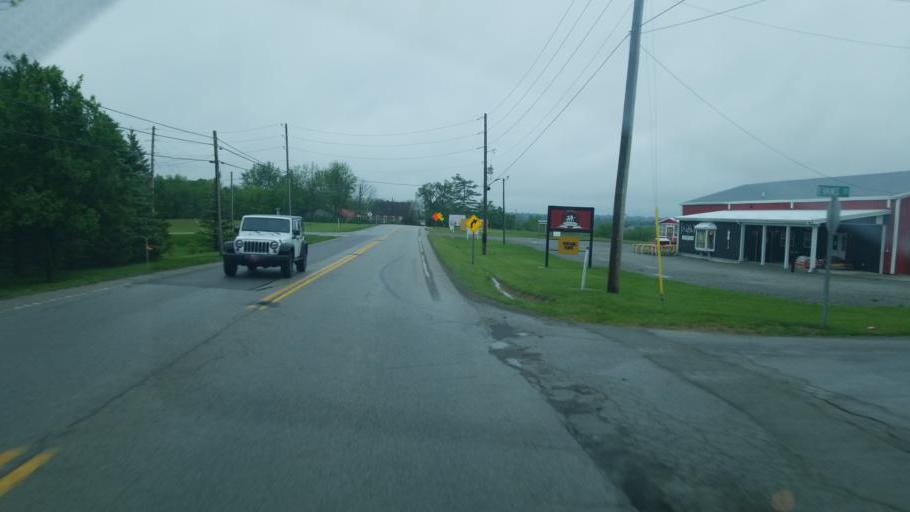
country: US
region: Ohio
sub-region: Highland County
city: Hillsboro
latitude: 39.2449
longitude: -83.6053
